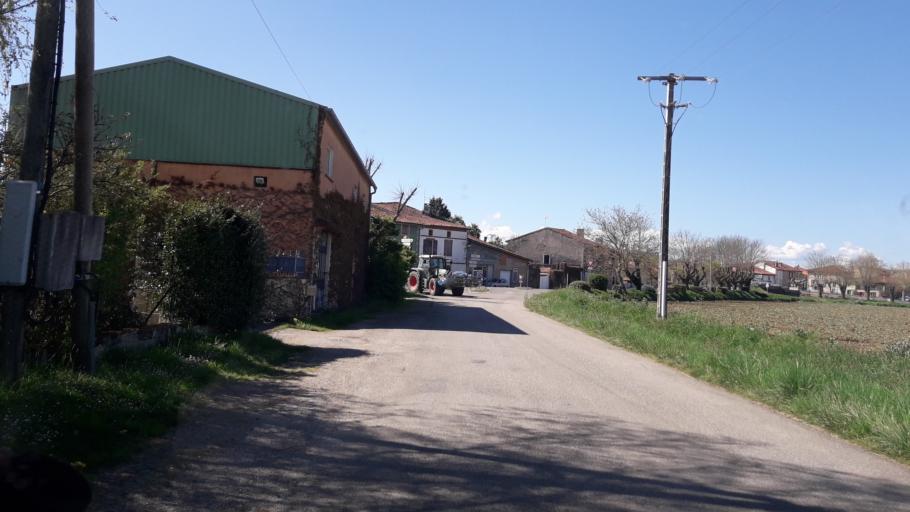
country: FR
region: Midi-Pyrenees
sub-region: Departement de la Haute-Garonne
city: Montesquieu-Volvestre
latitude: 43.1453
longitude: 1.3114
